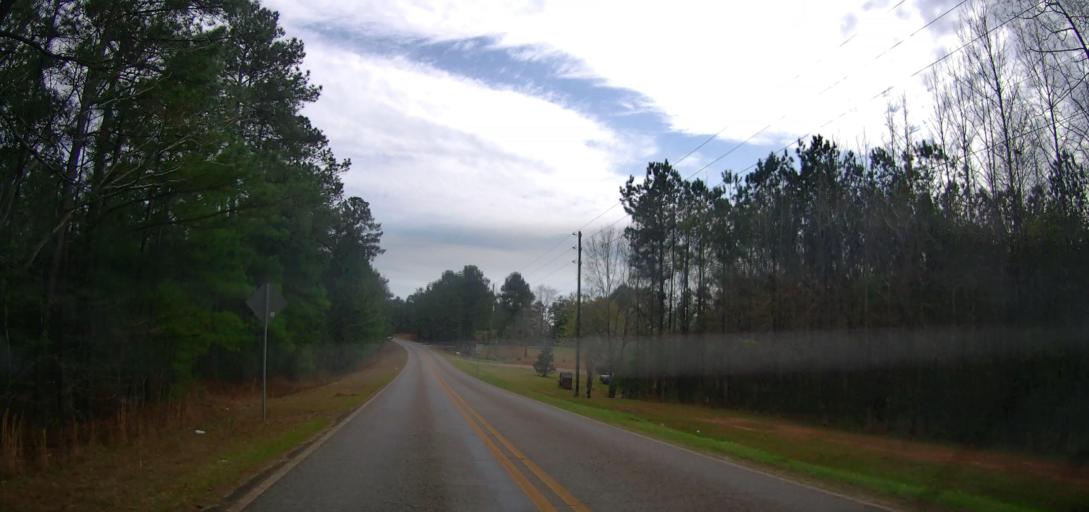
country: US
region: Georgia
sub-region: Bibb County
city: Macon
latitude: 32.9693
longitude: -83.6653
